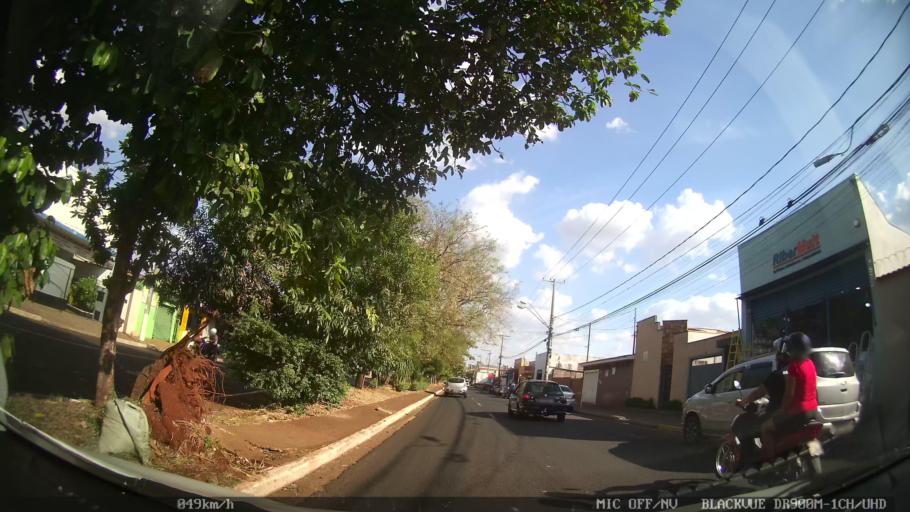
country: BR
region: Sao Paulo
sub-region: Ribeirao Preto
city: Ribeirao Preto
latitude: -21.1916
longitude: -47.8374
